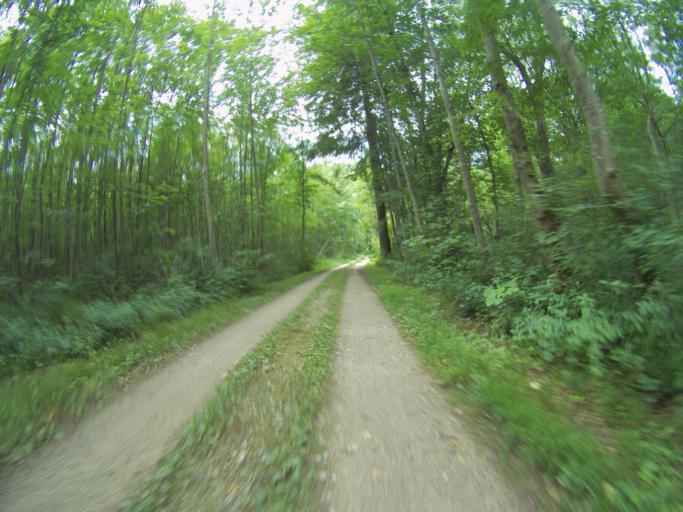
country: DE
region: Bavaria
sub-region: Upper Bavaria
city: Freising
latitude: 48.3657
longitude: 11.7339
